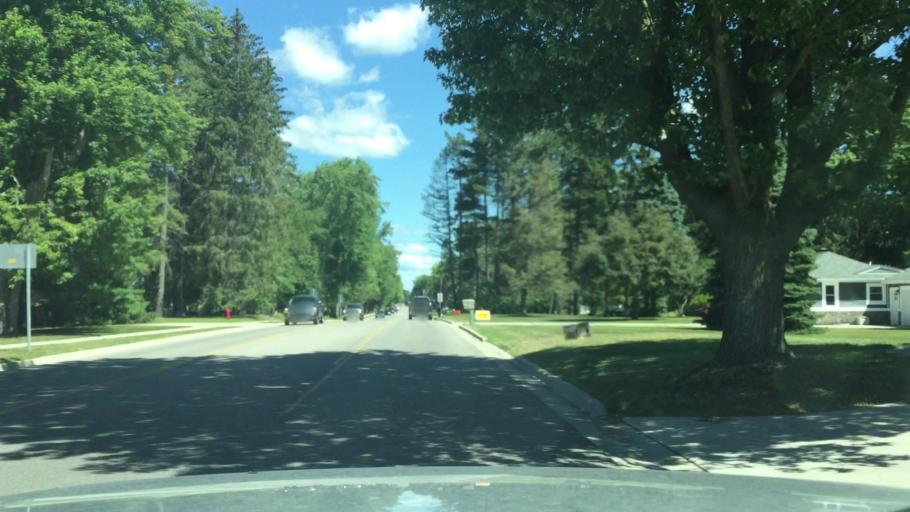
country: US
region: Michigan
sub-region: Saginaw County
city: Shields
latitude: 43.4188
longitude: -84.0714
